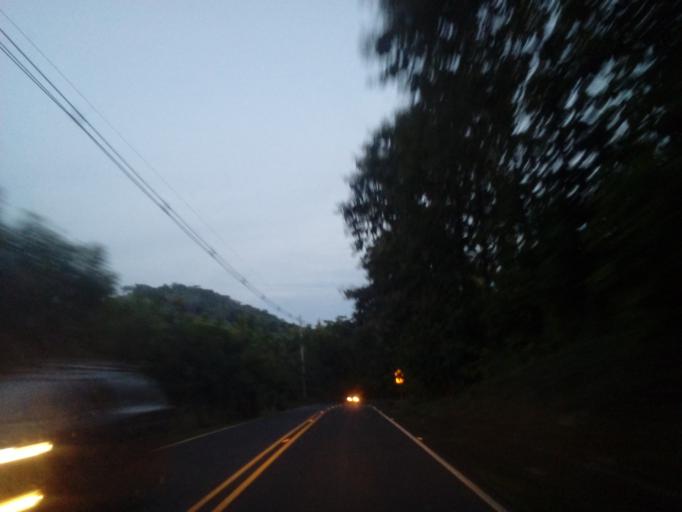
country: CR
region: Guanacaste
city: Samara
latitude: 9.9459
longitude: -85.5206
